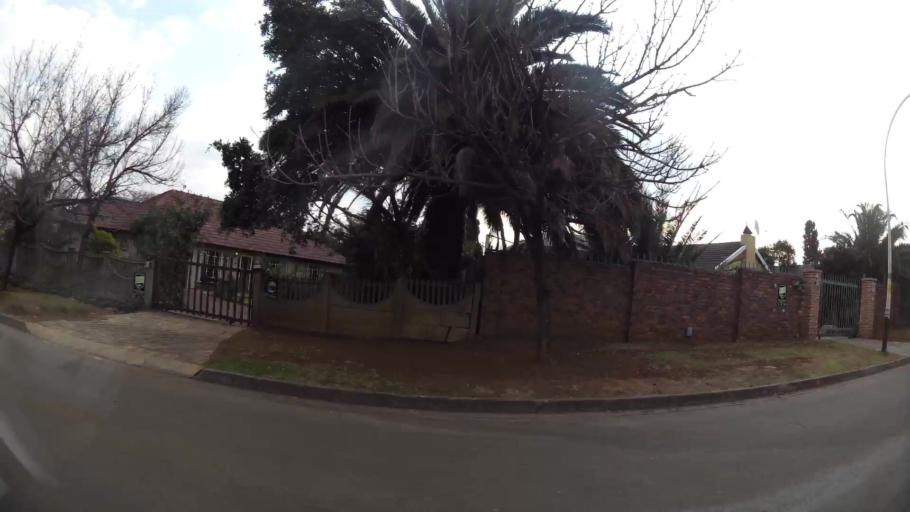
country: ZA
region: Gauteng
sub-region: City of Johannesburg Metropolitan Municipality
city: Modderfontein
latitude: -26.1386
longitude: 28.1853
